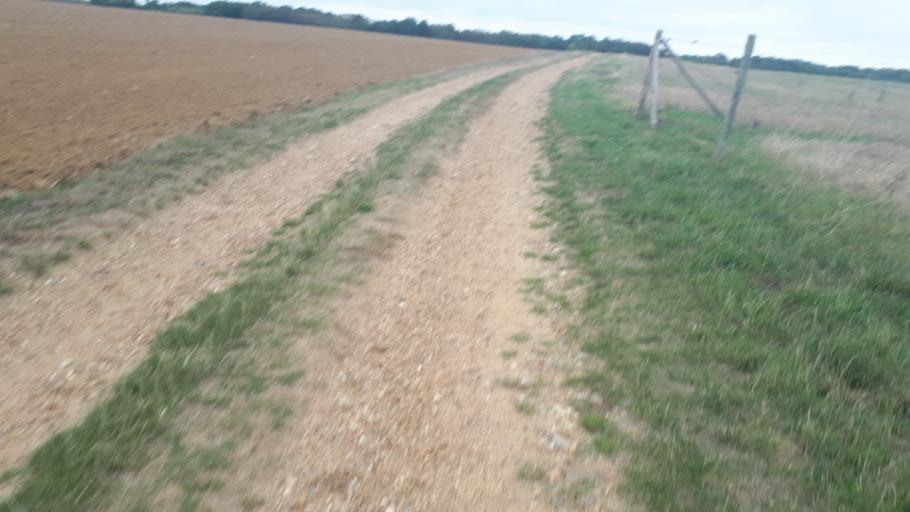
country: FR
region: Centre
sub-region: Departement du Loir-et-Cher
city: Villiers-sur-Loir
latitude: 47.8171
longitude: 0.9921
